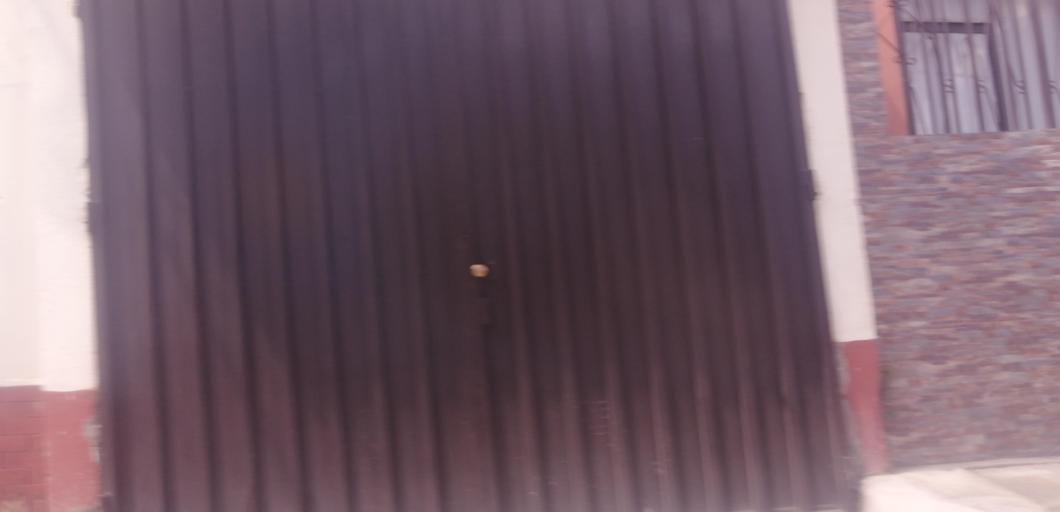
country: GT
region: Quetzaltenango
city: Quetzaltenango
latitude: 14.8268
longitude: -91.5335
